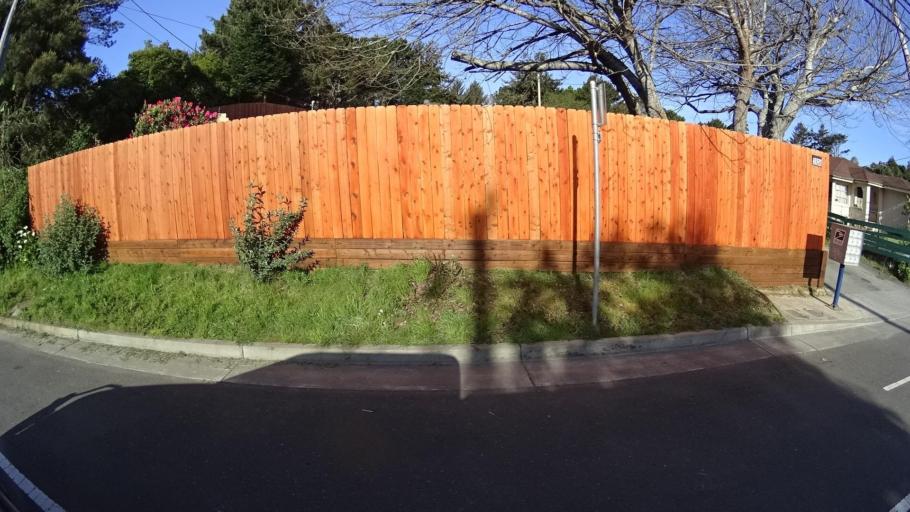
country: US
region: California
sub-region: Humboldt County
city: Bayview
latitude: 40.7721
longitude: -124.1740
